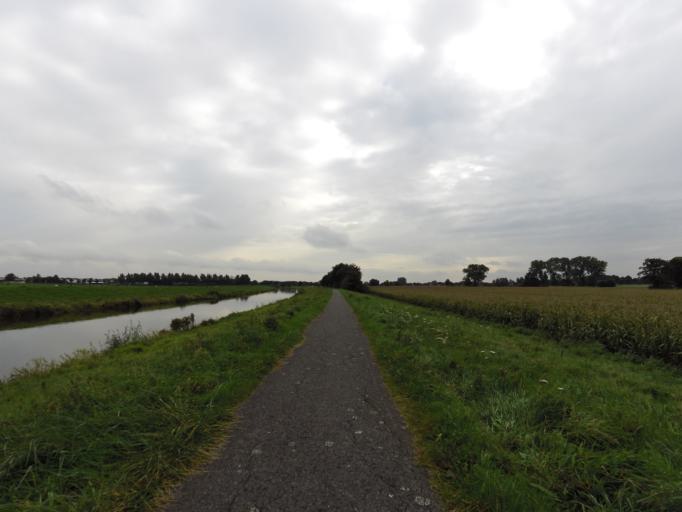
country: DE
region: North Rhine-Westphalia
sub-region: Regierungsbezirk Munster
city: Isselburg
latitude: 51.8587
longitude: 6.4577
